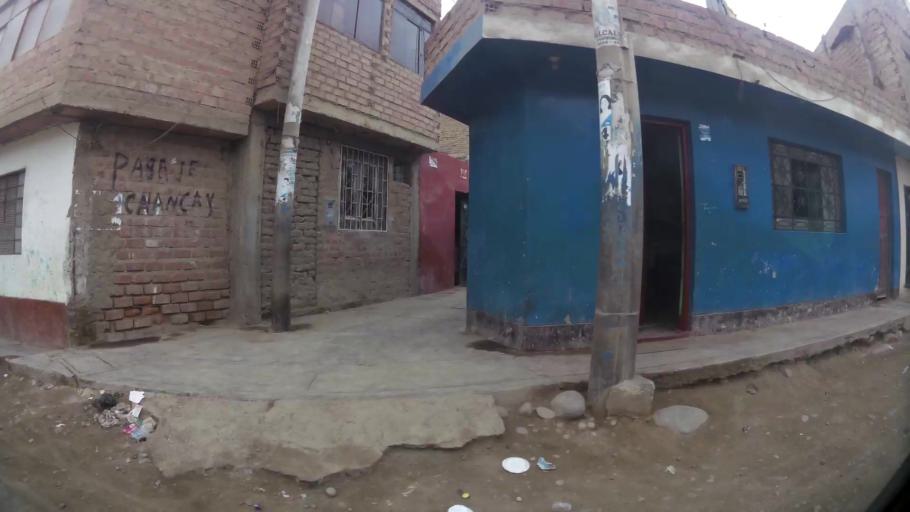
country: PE
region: Lima
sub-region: Provincia de Huaral
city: Huaral
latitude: -11.4992
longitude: -77.2038
